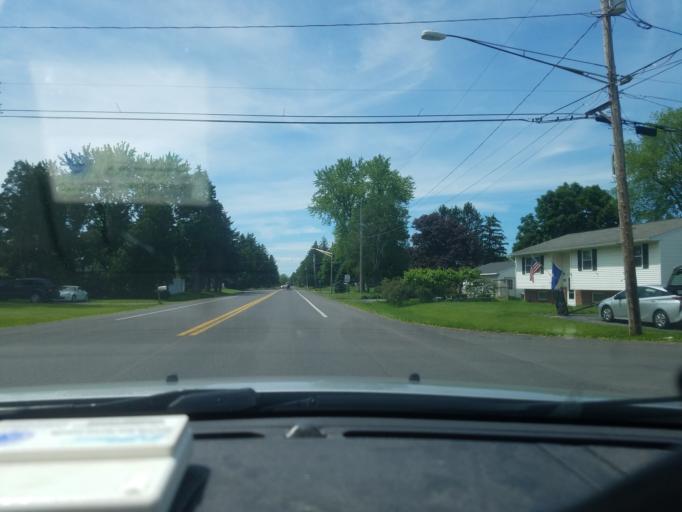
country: US
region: New York
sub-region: Onondaga County
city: East Syracuse
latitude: 43.0804
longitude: -76.0714
